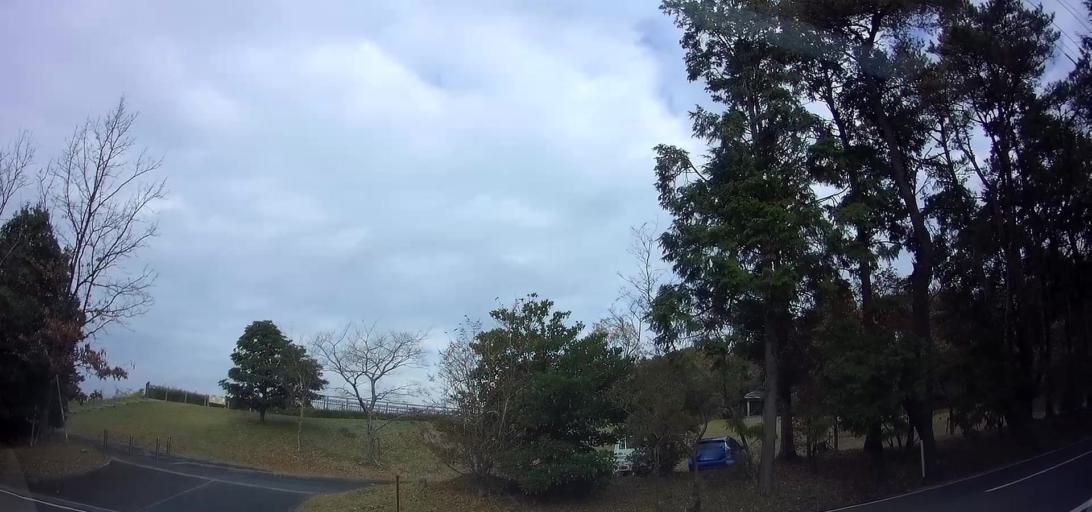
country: JP
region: Nagasaki
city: Shimabara
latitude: 32.7040
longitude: 130.2412
